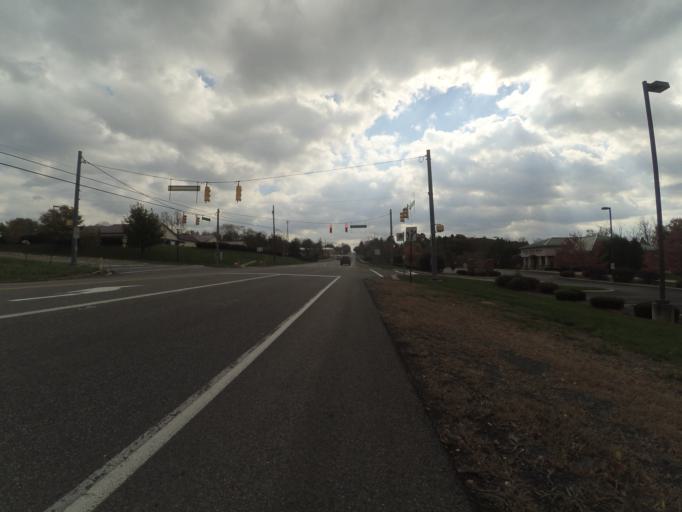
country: US
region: Pennsylvania
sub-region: Centre County
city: Bellefonte
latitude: 40.8962
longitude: -77.7875
